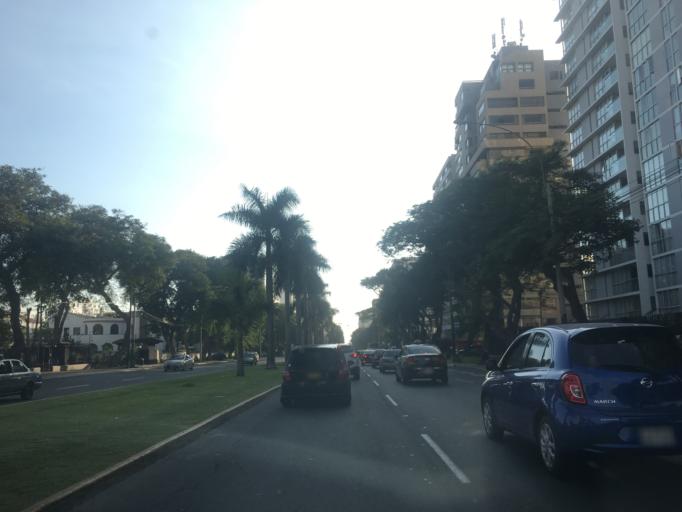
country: PE
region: Lima
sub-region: Lima
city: San Isidro
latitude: -12.0932
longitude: -77.0405
